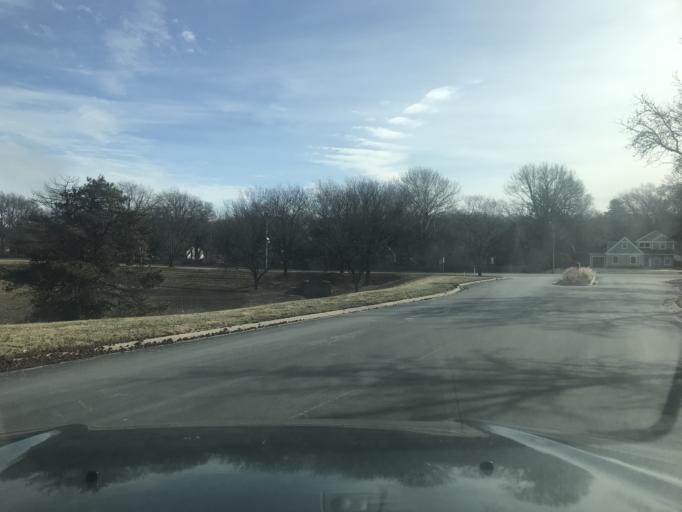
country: US
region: Kansas
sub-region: Johnson County
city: Fairway
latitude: 39.0277
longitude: -94.6365
